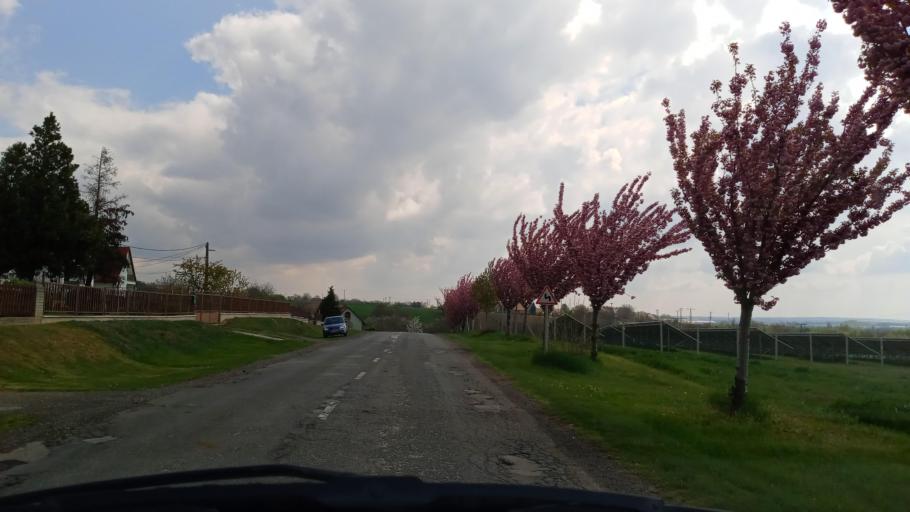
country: HU
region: Baranya
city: Pecsvarad
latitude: 46.1070
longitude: 18.5231
